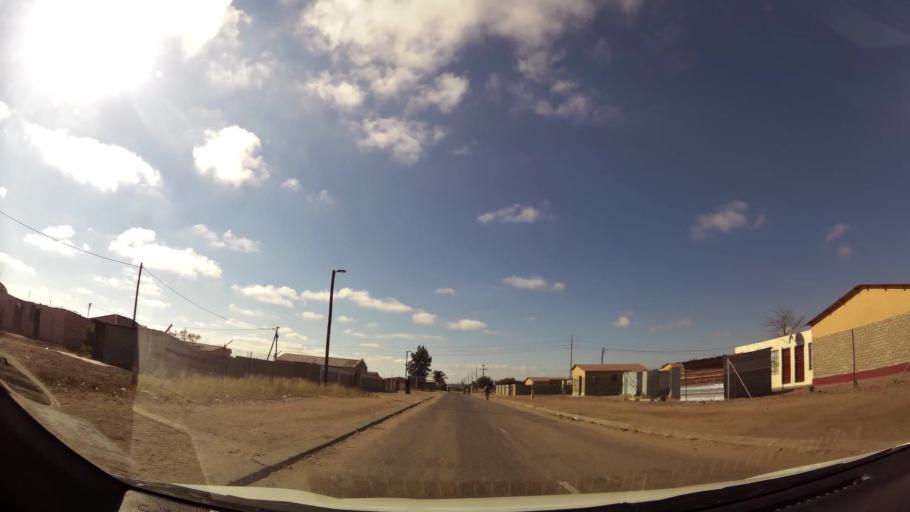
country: ZA
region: Limpopo
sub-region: Capricorn District Municipality
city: Polokwane
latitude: -23.8477
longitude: 29.4001
